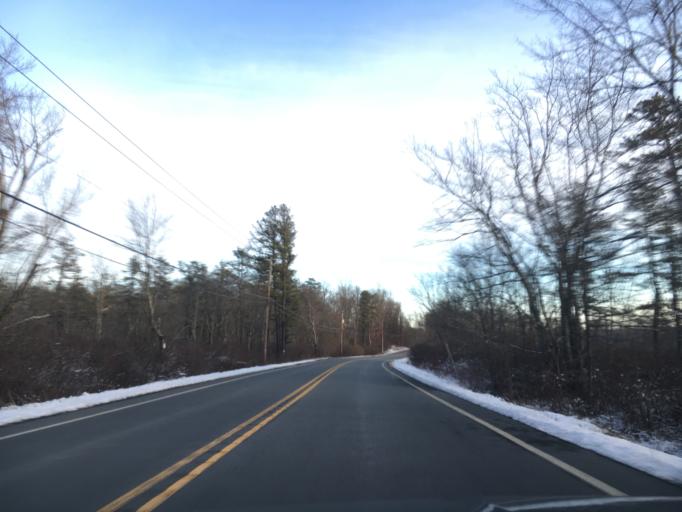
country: US
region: Pennsylvania
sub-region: Pike County
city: Hemlock Farms
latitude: 41.2568
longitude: -75.0772
